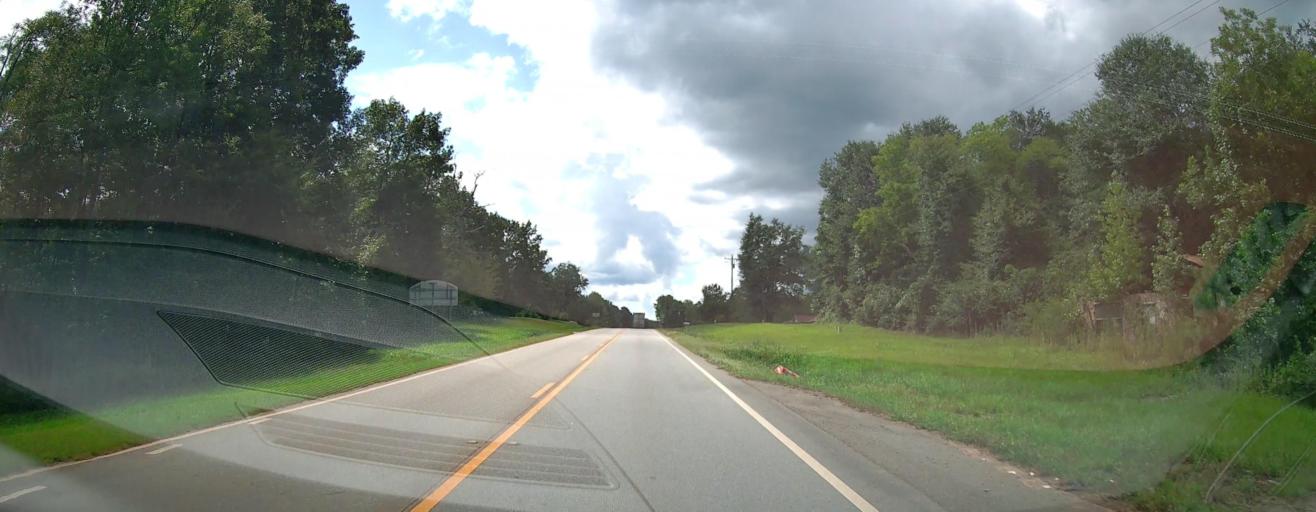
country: US
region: Georgia
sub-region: Bibb County
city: West Point
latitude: 32.8647
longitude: -83.8611
